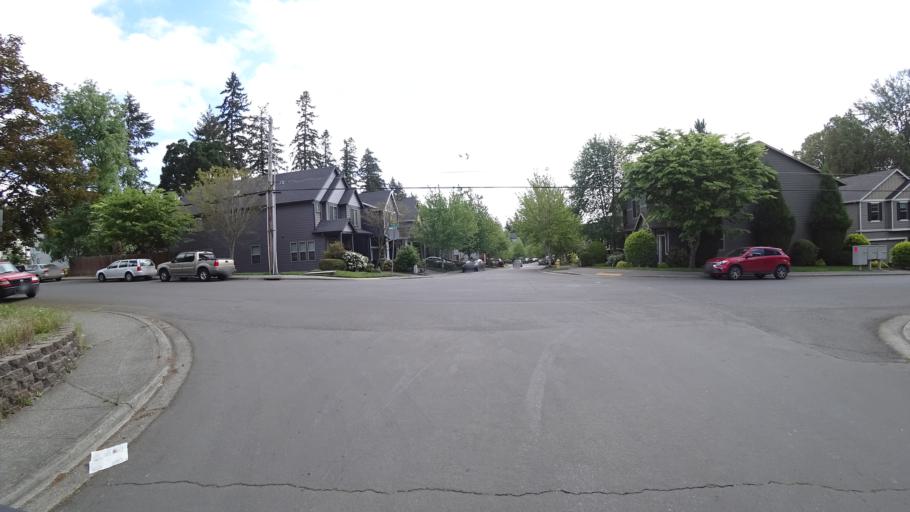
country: US
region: Oregon
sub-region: Washington County
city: Aloha
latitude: 45.5121
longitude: -122.8839
